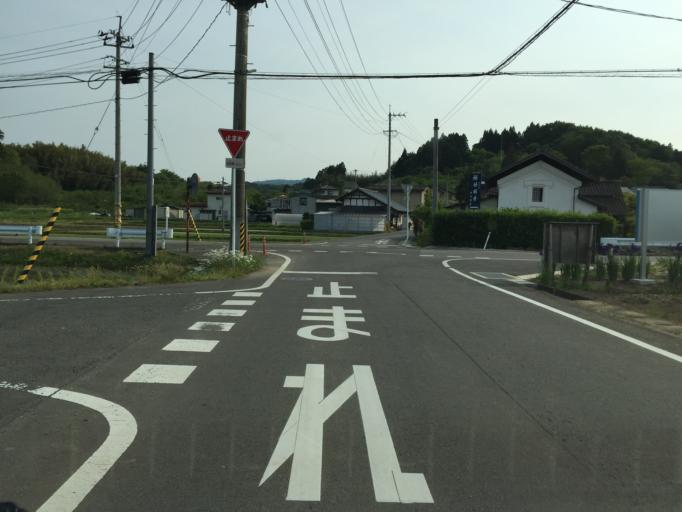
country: JP
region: Fukushima
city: Fukushima-shi
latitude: 37.7193
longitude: 140.4310
